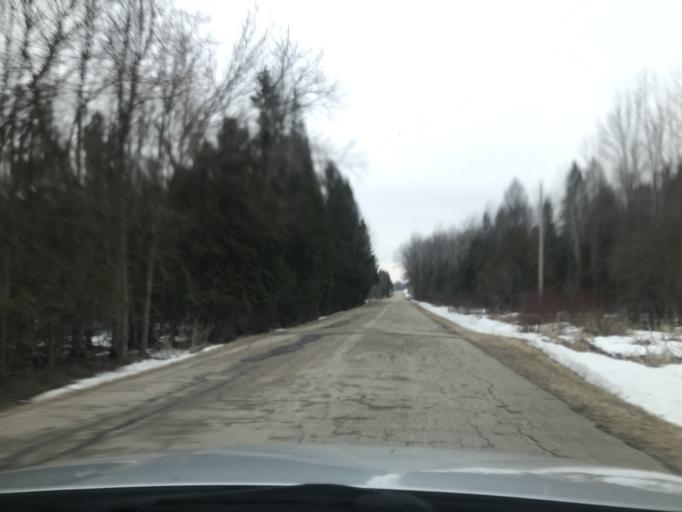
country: US
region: Wisconsin
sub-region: Marinette County
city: Peshtigo
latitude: 45.1175
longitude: -88.0081
